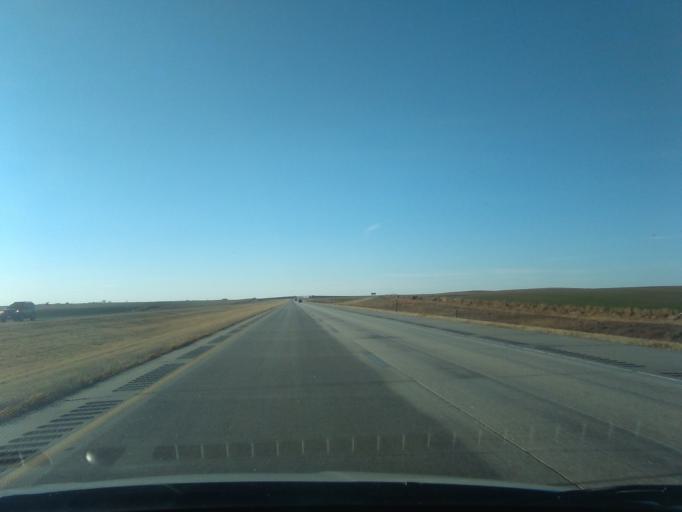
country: US
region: Nebraska
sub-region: Cheyenne County
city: Sidney
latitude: 41.1131
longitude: -102.8299
